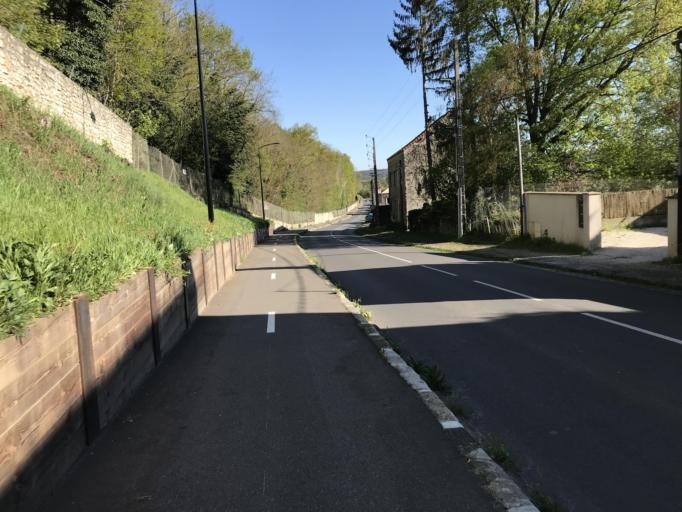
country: FR
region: Ile-de-France
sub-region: Departement de l'Essonne
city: Marcoussis
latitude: 48.6527
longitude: 2.2135
